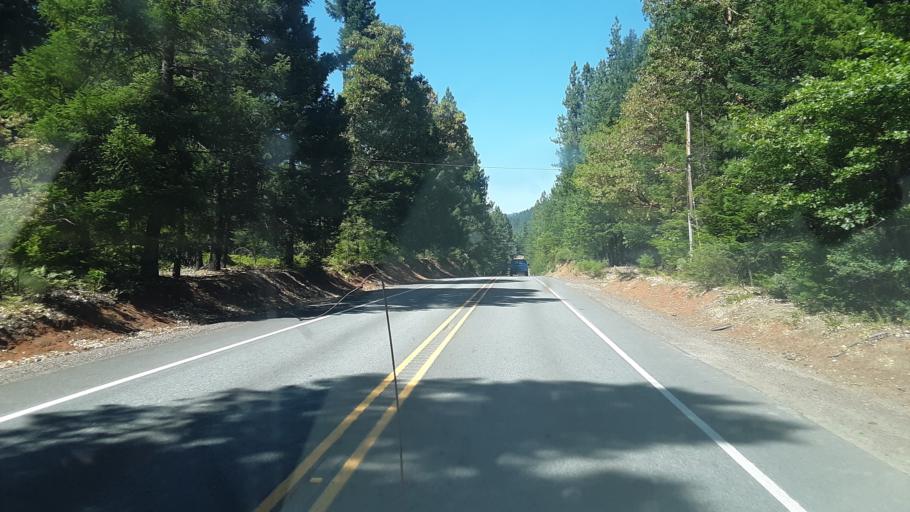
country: US
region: Oregon
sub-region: Josephine County
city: Cave Junction
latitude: 42.3042
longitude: -123.6109
